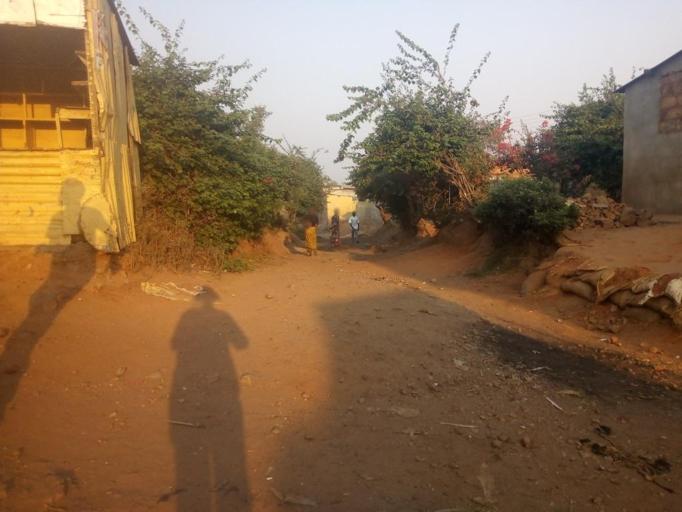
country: ZM
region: Lusaka
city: Lusaka
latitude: -15.4069
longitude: 28.3644
